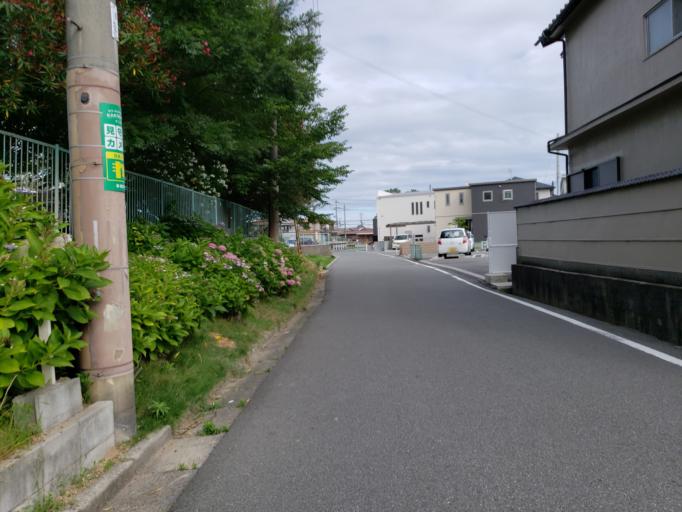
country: JP
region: Hyogo
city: Kakogawacho-honmachi
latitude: 34.7657
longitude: 134.8233
